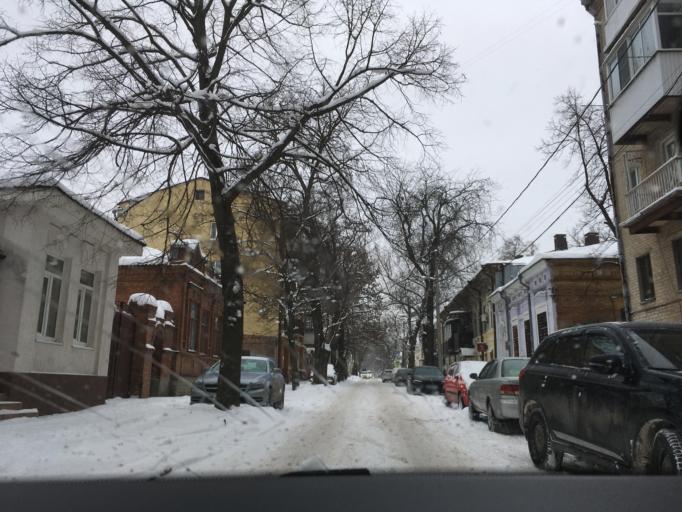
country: RU
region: Rostov
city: Rostov-na-Donu
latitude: 47.2296
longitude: 39.7543
